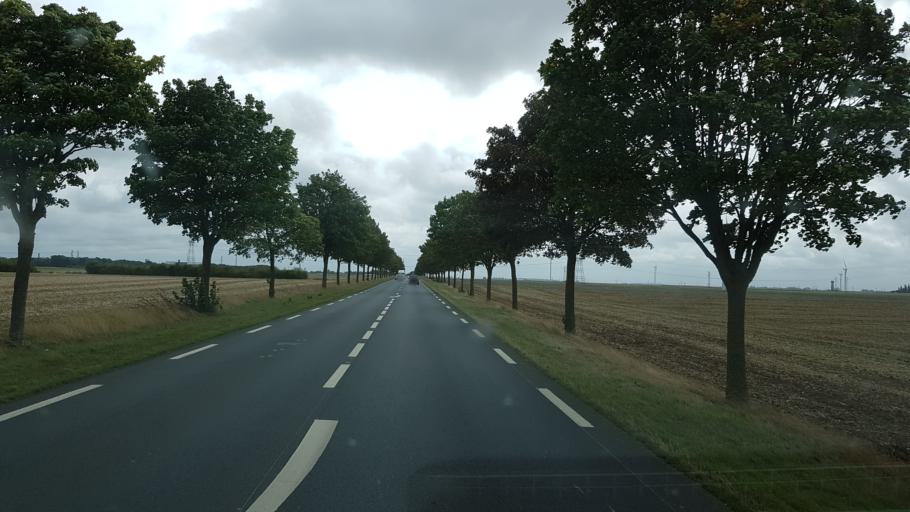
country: FR
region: Centre
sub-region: Departement d'Eure-et-Loir
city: Janville
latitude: 48.1970
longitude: 1.8927
